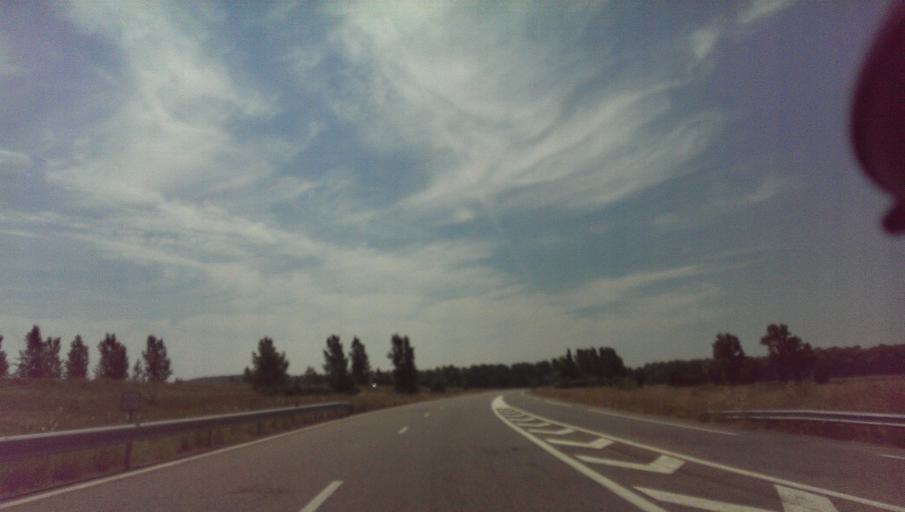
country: FR
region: Midi-Pyrenees
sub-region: Departement de la Haute-Garonne
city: Villenouvelle
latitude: 43.4182
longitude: 1.6525
